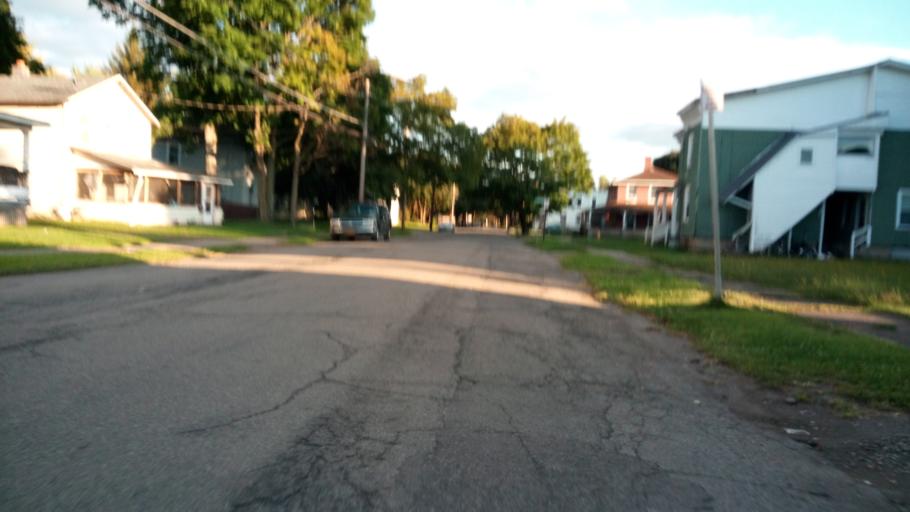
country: US
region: New York
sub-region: Chemung County
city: Elmira
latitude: 42.1022
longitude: -76.8019
